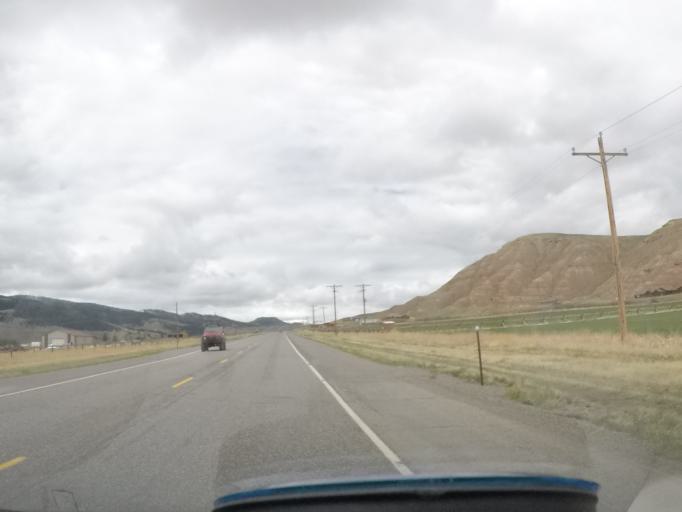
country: US
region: Wyoming
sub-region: Sublette County
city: Pinedale
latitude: 43.5690
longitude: -109.7133
